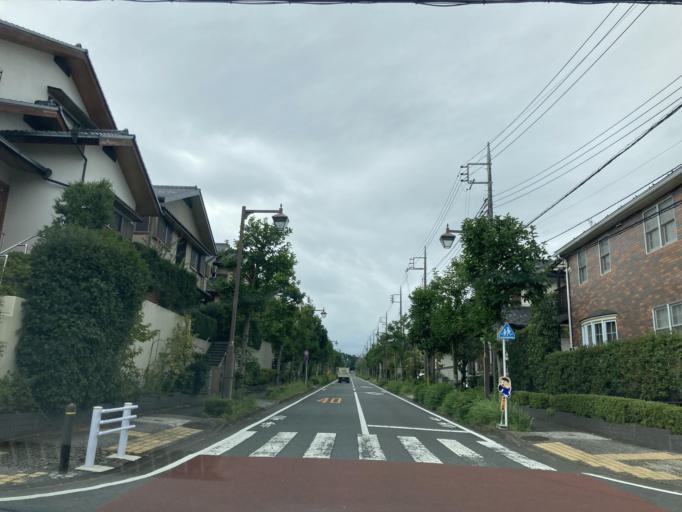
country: JP
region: Tokyo
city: Chofugaoka
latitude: 35.6369
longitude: 139.4922
